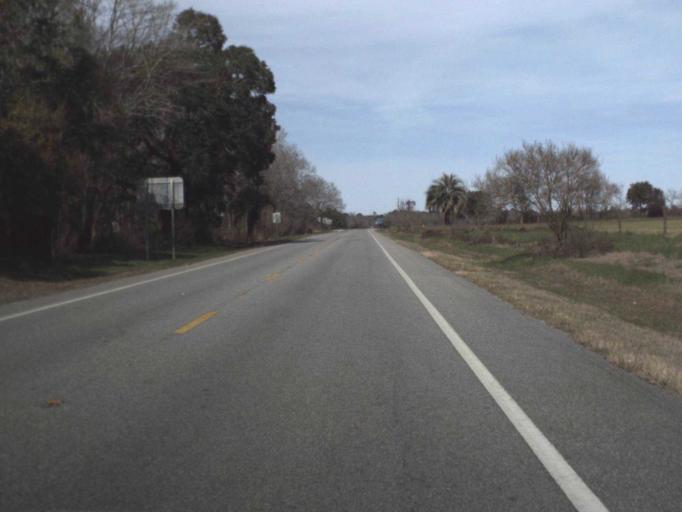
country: US
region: Florida
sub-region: Jackson County
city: Graceville
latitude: 30.9946
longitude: -85.4792
